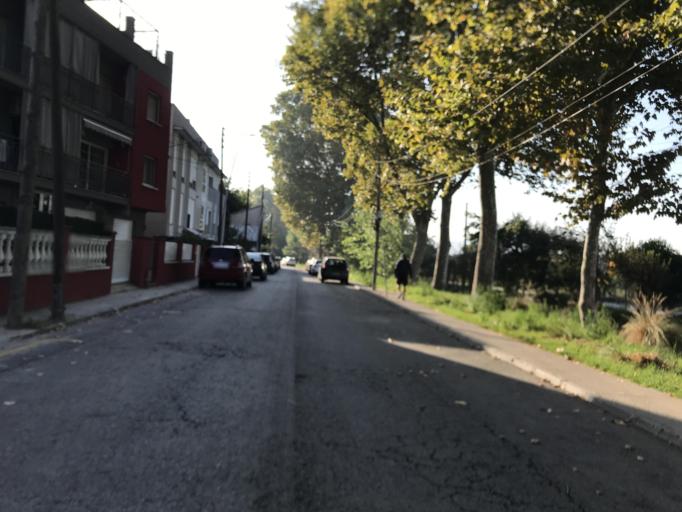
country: ES
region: Catalonia
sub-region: Provincia de Barcelona
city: Mollet del Valles
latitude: 41.5556
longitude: 2.2201
